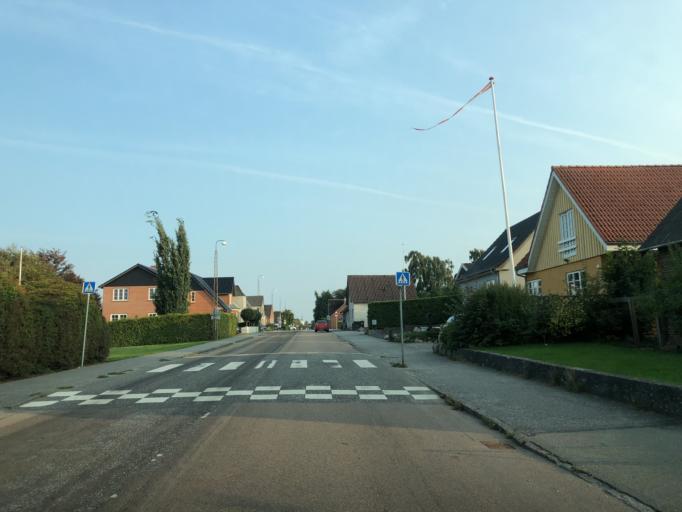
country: DK
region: South Denmark
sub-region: Vejle Kommune
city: Jelling
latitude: 55.7106
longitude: 9.3743
